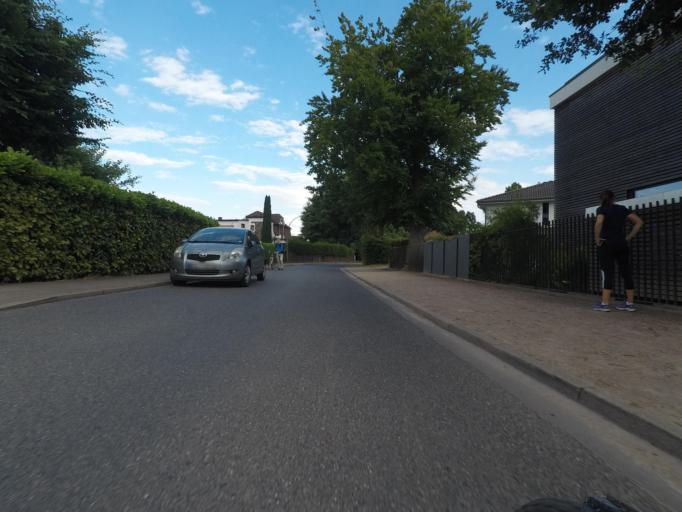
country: DE
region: Hamburg
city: Sasel
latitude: 53.6352
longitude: 10.1137
